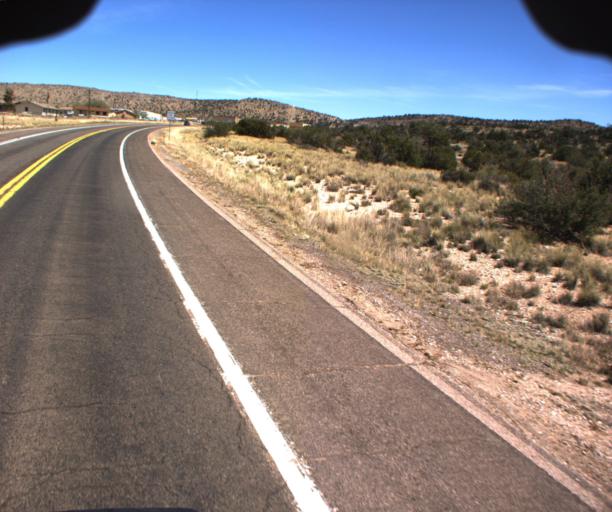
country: US
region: Arizona
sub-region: Mohave County
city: Peach Springs
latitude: 35.5384
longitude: -113.4184
